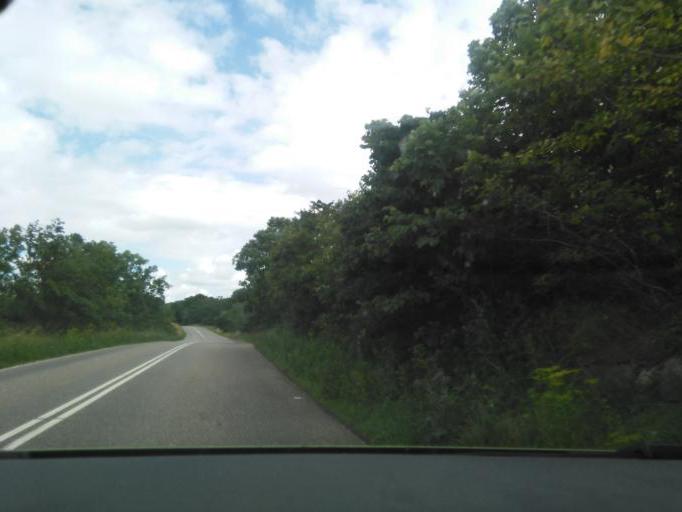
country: DK
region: Zealand
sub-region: Kalundborg Kommune
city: Hong
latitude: 55.5567
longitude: 11.3098
